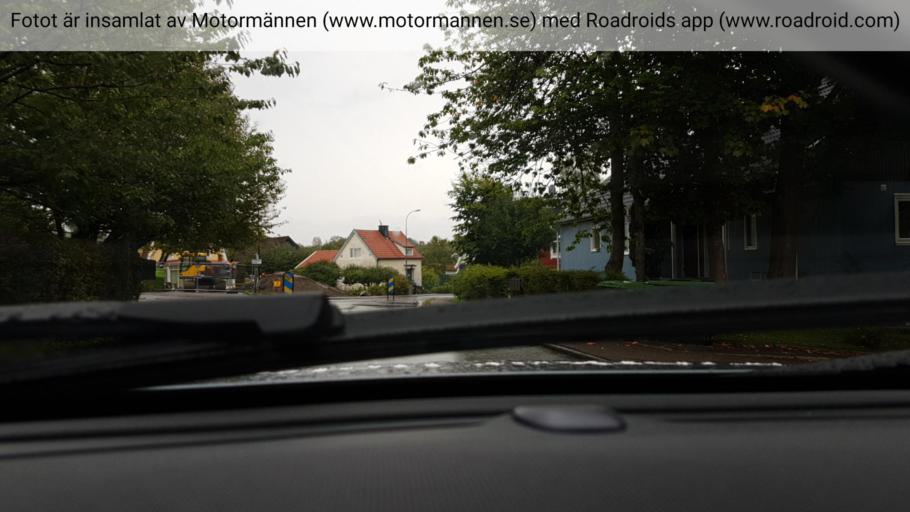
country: SE
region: Vaestra Goetaland
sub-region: Molndal
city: Moelndal
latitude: 57.6737
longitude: 11.9951
